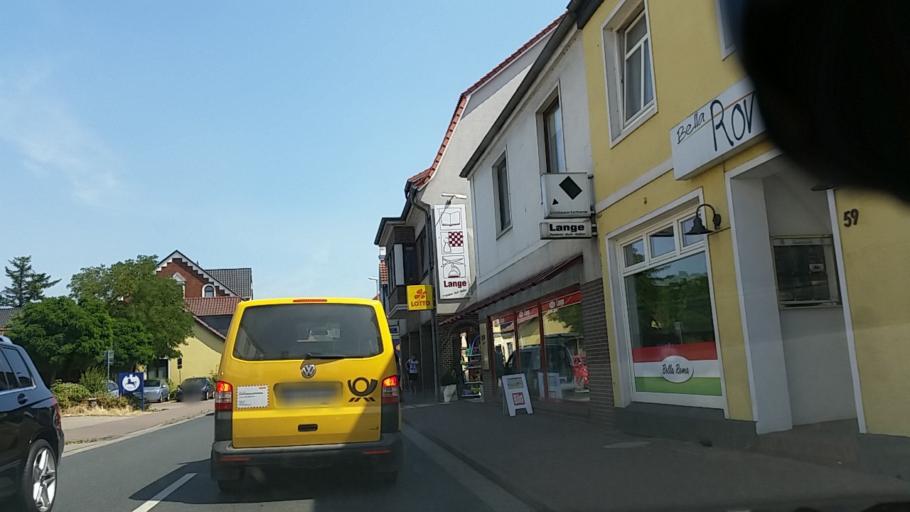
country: DE
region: Lower Saxony
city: Thedinghausen
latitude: 52.9622
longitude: 9.0215
